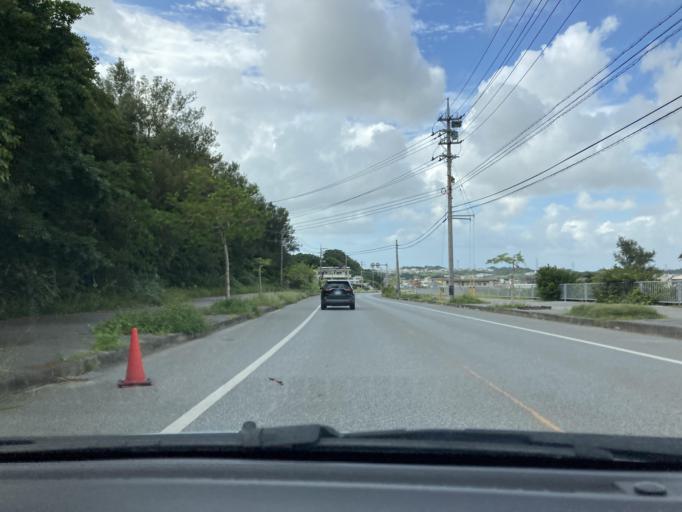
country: JP
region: Okinawa
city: Itoman
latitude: 26.1275
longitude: 127.6907
